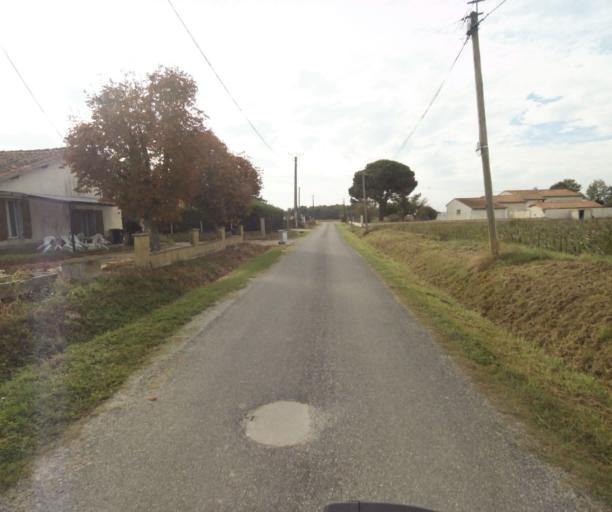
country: FR
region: Midi-Pyrenees
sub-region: Departement du Tarn-et-Garonne
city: Montech
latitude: 43.9429
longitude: 1.2326
